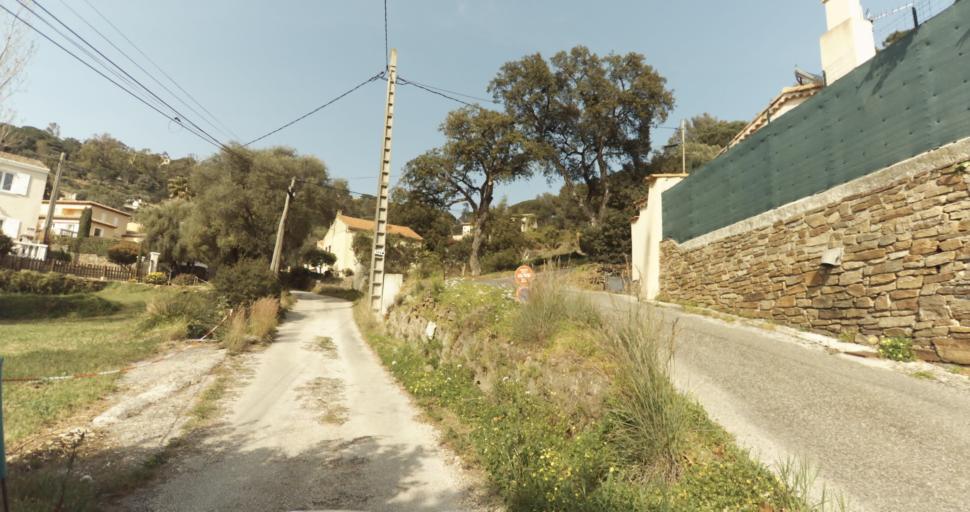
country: FR
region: Provence-Alpes-Cote d'Azur
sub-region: Departement du Var
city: Bormes-les-Mimosas
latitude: 43.1469
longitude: 6.3442
